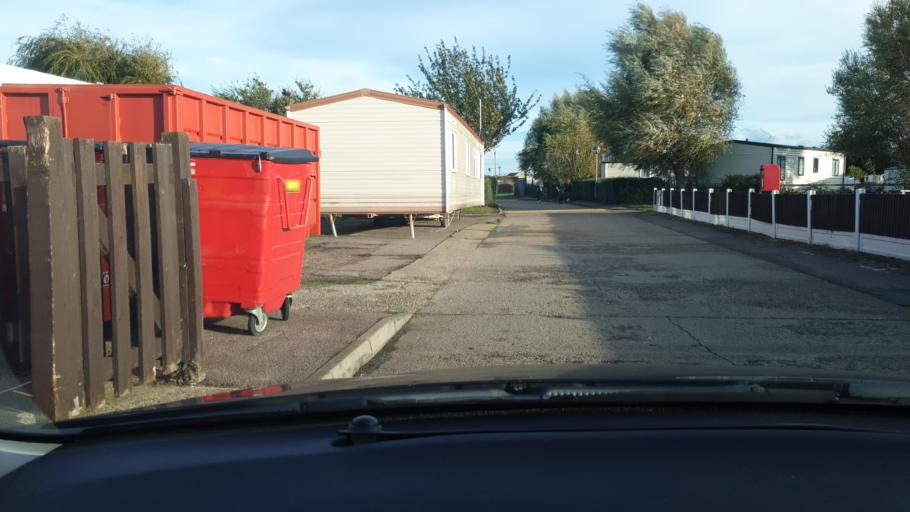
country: GB
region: England
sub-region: Essex
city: Brightlingsea
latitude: 51.7995
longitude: 1.0244
